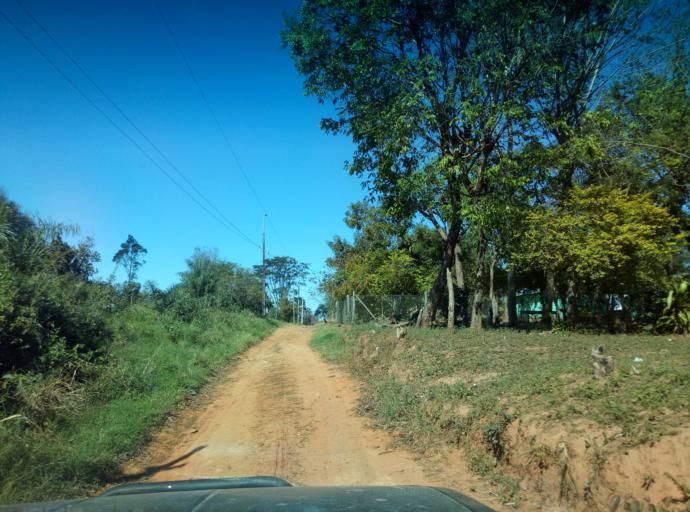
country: PY
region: Caaguazu
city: Doctor Cecilio Baez
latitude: -25.1774
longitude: -56.2020
